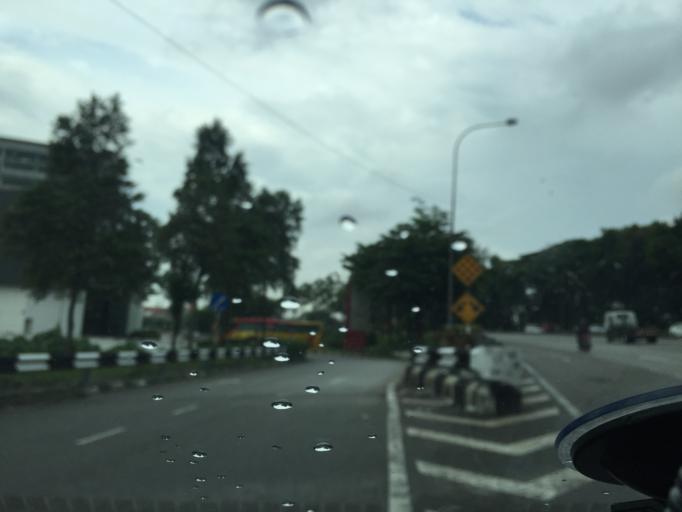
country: MY
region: Selangor
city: Klang
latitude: 3.0061
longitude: 101.4420
